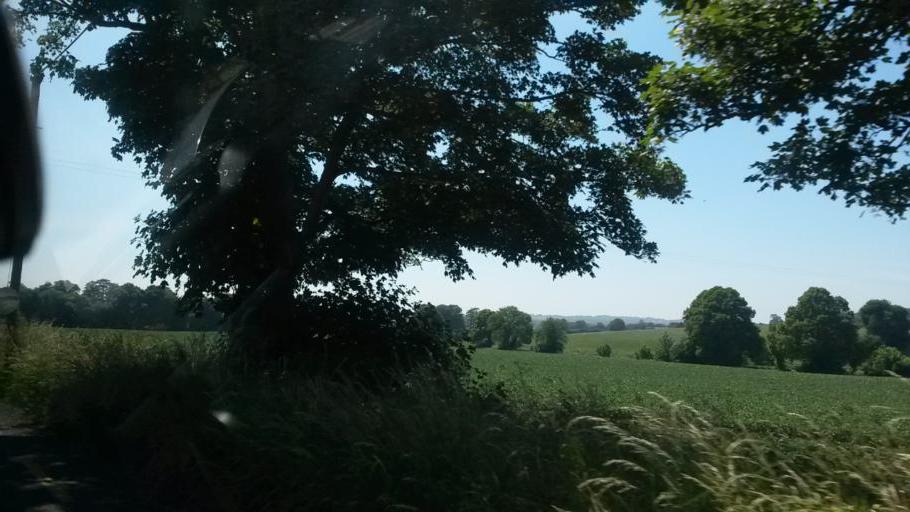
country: IE
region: Leinster
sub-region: An Mhi
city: Stamullin
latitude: 53.5785
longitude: -6.3110
